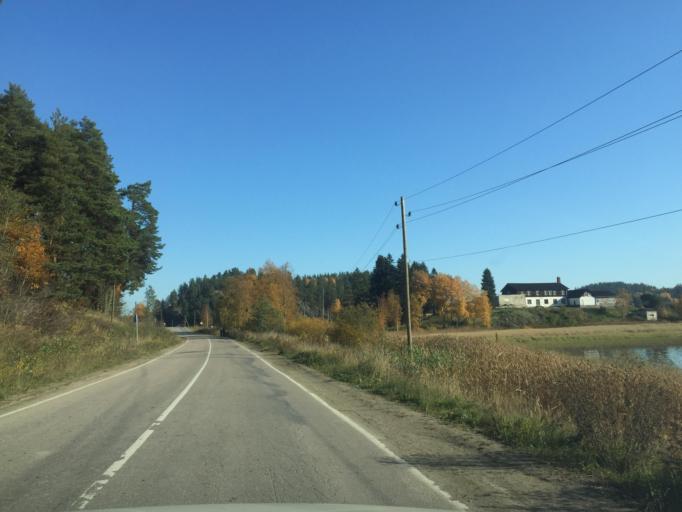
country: RU
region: Leningrad
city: Kuznechnoye
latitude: 61.2985
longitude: 29.9043
